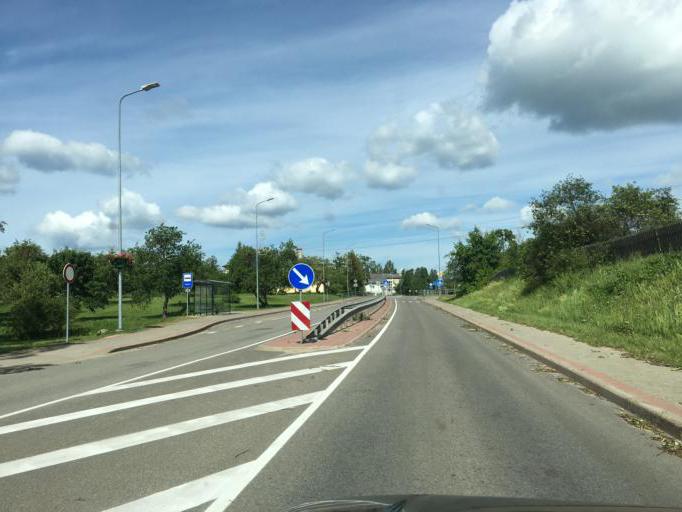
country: LV
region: Balvu Rajons
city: Balvi
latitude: 57.1381
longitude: 27.2546
